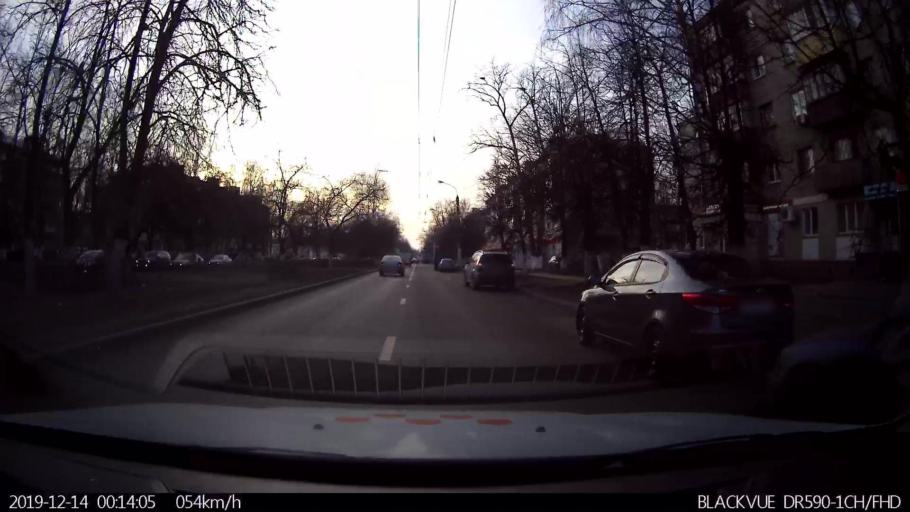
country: RU
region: Nizjnij Novgorod
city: Burevestnik
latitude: 56.2338
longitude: 43.8577
